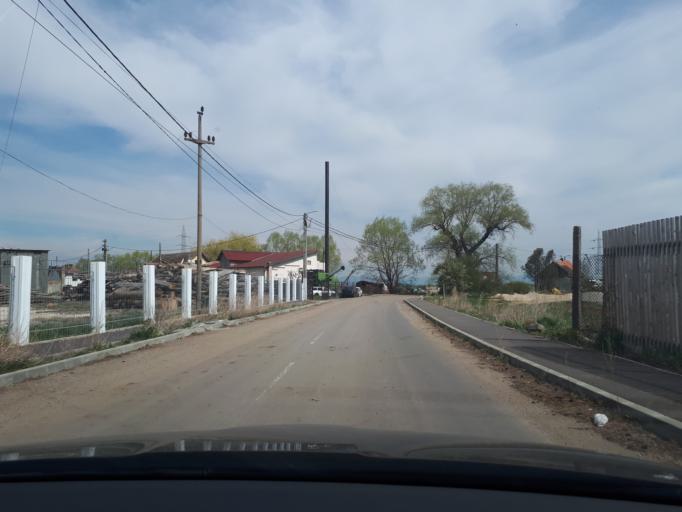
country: RO
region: Brasov
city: Codlea
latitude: 45.7043
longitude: 25.4624
